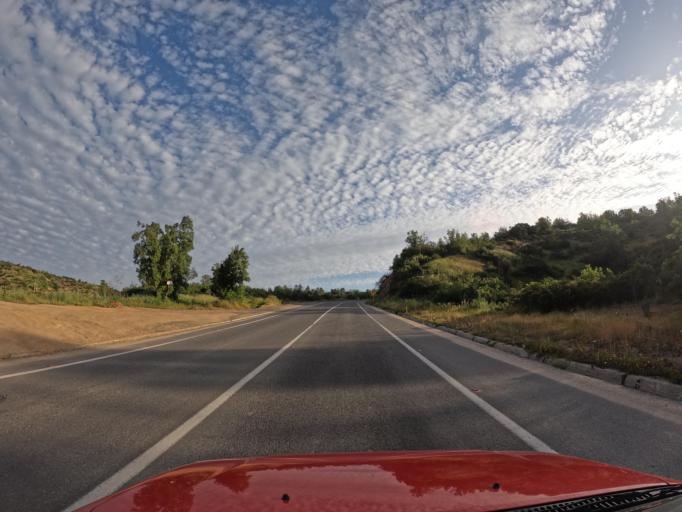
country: CL
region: Valparaiso
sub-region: San Antonio Province
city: San Antonio
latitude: -34.0456
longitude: -71.5932
